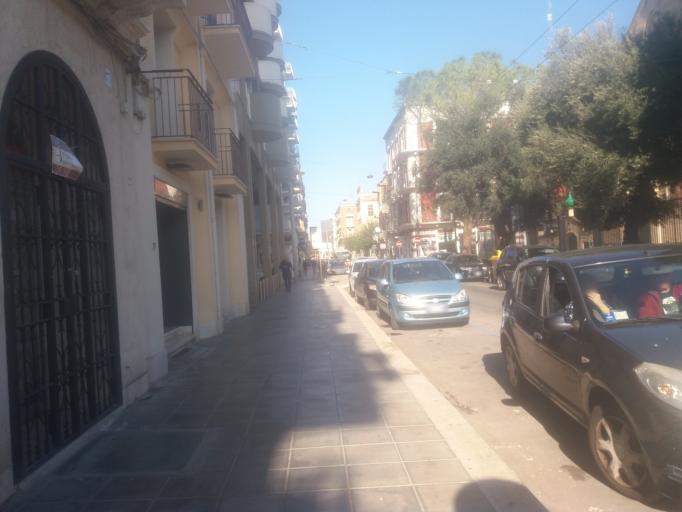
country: IT
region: Apulia
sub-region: Provincia di Bari
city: Bari
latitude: 41.1100
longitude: 16.8720
